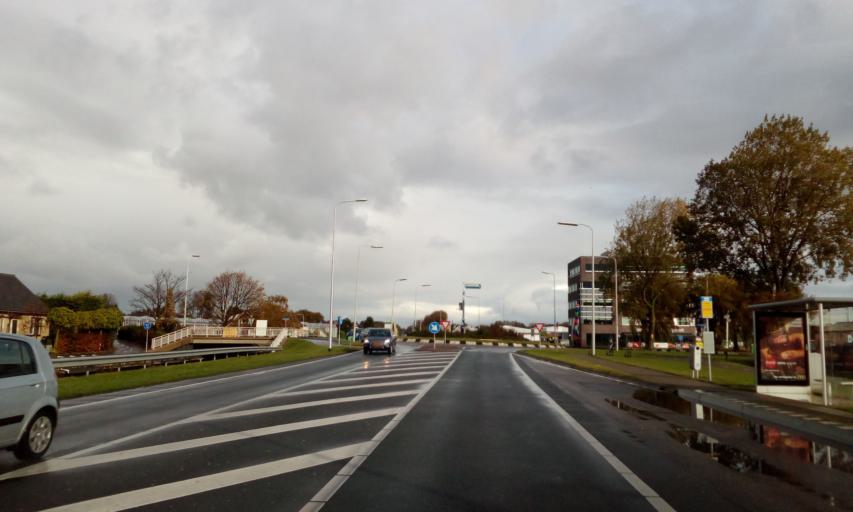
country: NL
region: South Holland
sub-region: Gemeente Westland
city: Poeldijk
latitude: 52.0315
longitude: 4.2241
